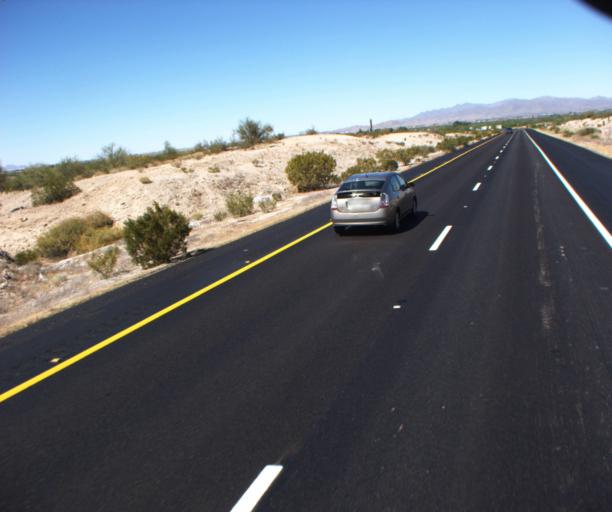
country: US
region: Arizona
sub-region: Maricopa County
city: Buckeye
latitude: 33.3131
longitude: -112.6240
